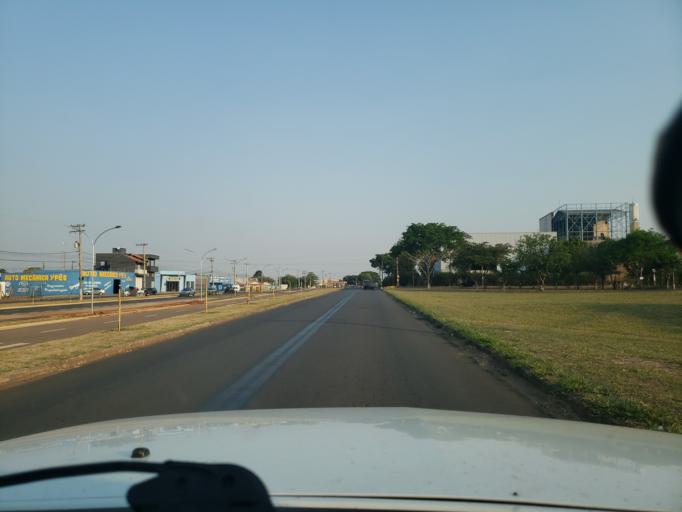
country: BR
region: Sao Paulo
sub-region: Moji-Guacu
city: Mogi-Gaucu
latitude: -22.3371
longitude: -46.9445
